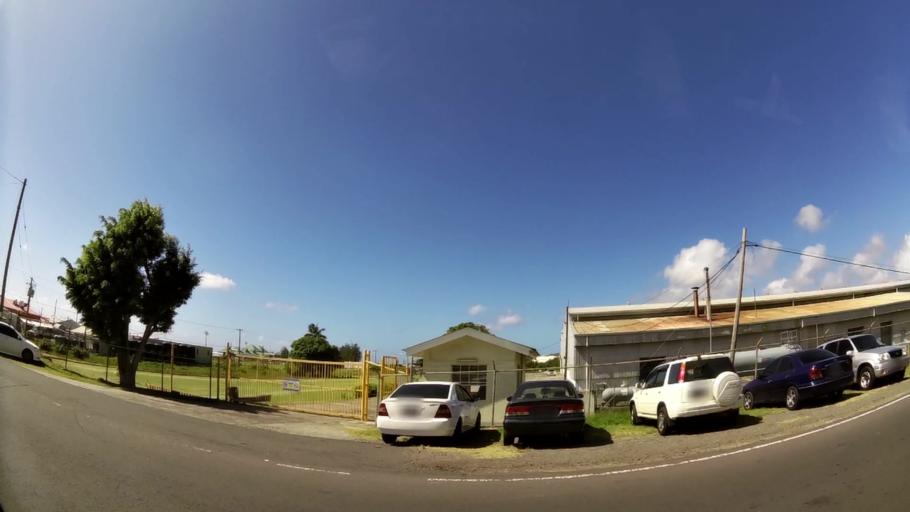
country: LC
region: Vieux-Fort
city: Vieux Fort
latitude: 13.7390
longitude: -60.9465
